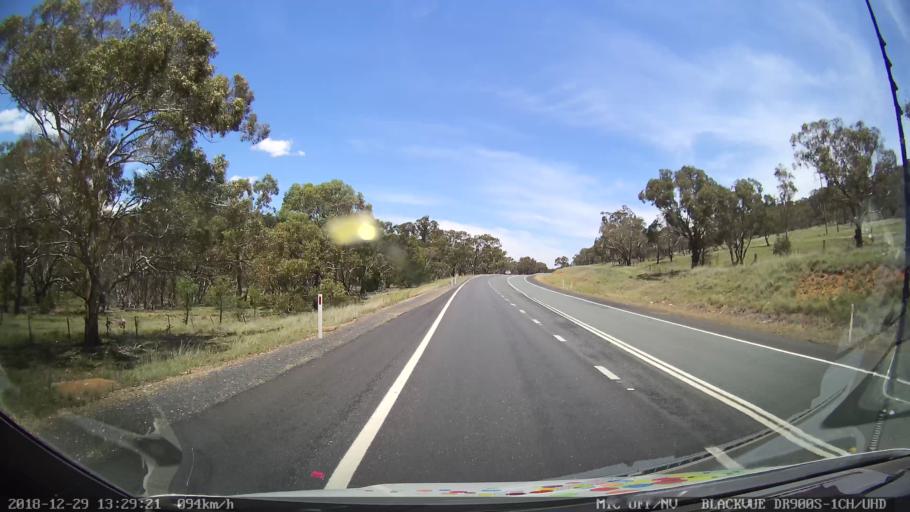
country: AU
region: New South Wales
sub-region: Cooma-Monaro
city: Cooma
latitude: -35.8889
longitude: 149.1618
